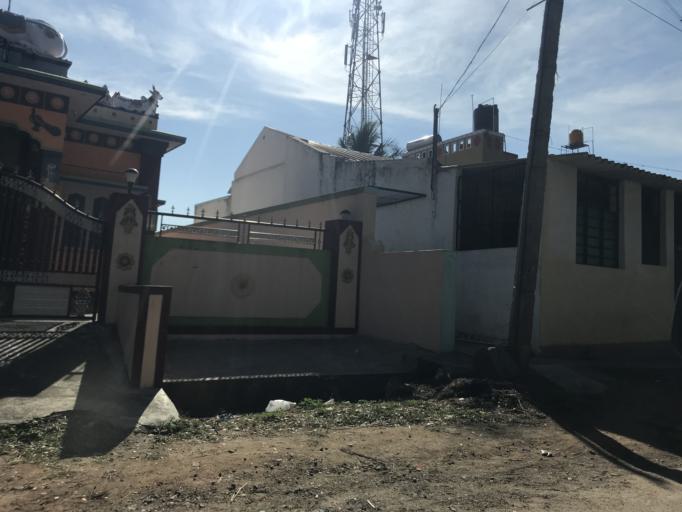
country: IN
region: Karnataka
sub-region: Mysore
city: Mysore
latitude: 12.2047
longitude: 76.5555
